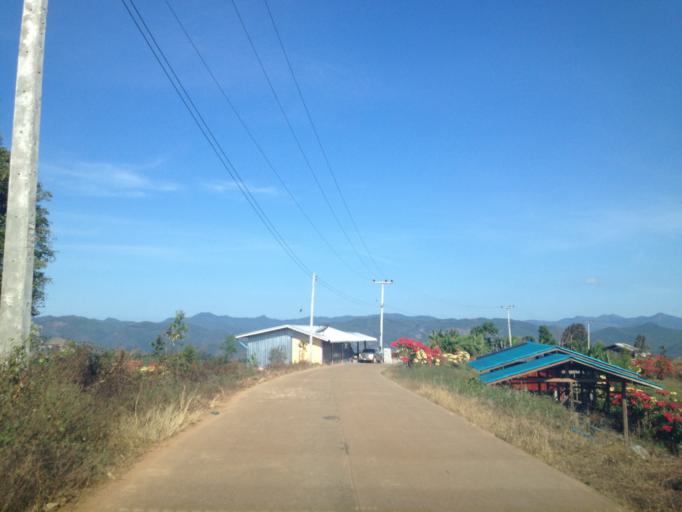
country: TH
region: Mae Hong Son
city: Ban Huai I Huak
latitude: 18.0441
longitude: 98.1654
